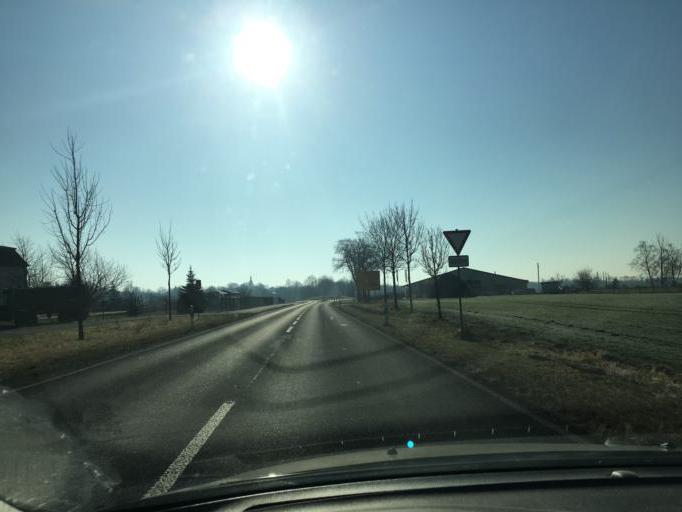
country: DE
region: Saxony
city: Bad Lausick
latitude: 51.1547
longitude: 12.6331
